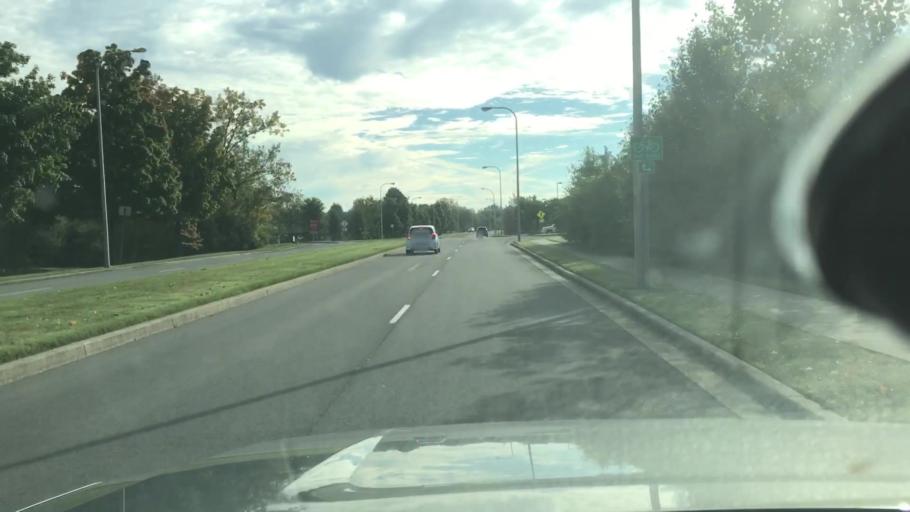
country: US
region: Tennessee
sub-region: Davidson County
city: Nashville
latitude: 36.1992
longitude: -86.7992
